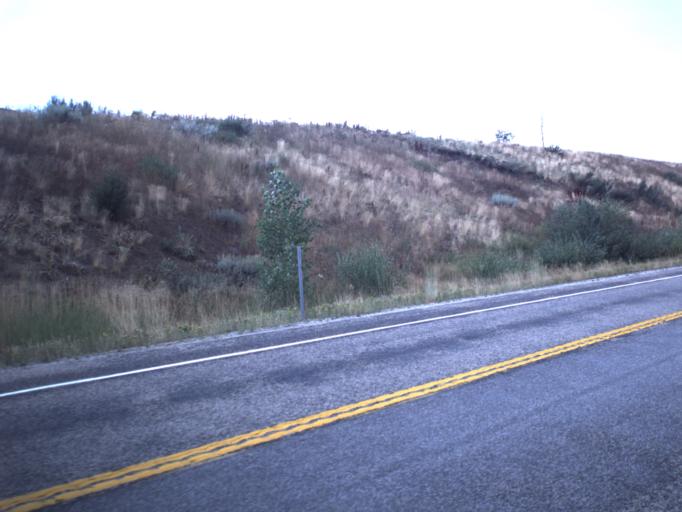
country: US
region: Utah
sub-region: Cache County
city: Richmond
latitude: 41.8778
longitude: -111.5643
